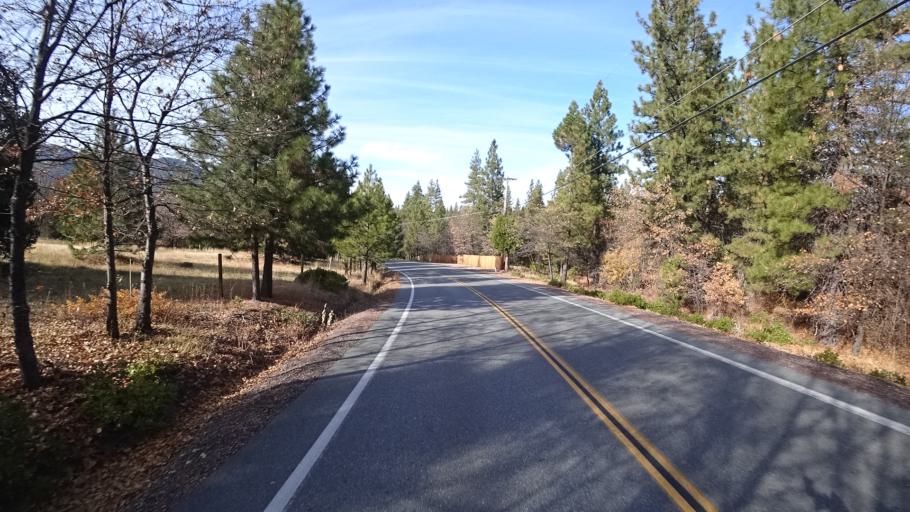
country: US
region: California
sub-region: Siskiyou County
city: Weed
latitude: 41.3965
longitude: -122.4139
